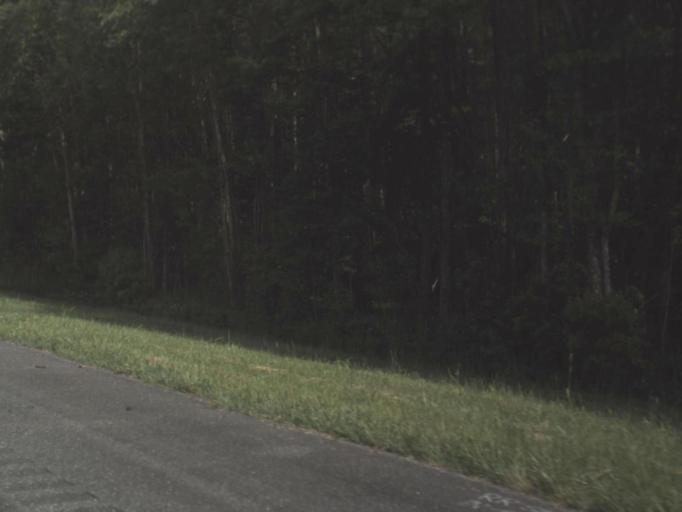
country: US
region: Florida
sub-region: Columbia County
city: Watertown
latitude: 30.2538
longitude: -82.4134
